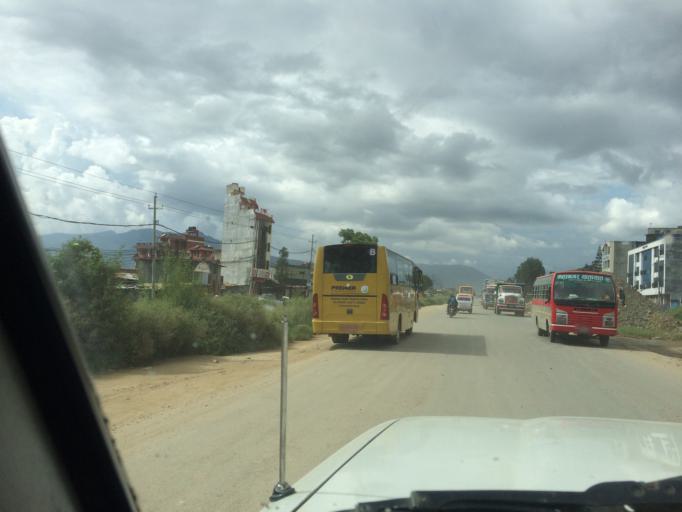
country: NP
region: Central Region
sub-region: Bagmati Zone
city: Patan
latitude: 27.6760
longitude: 85.3021
